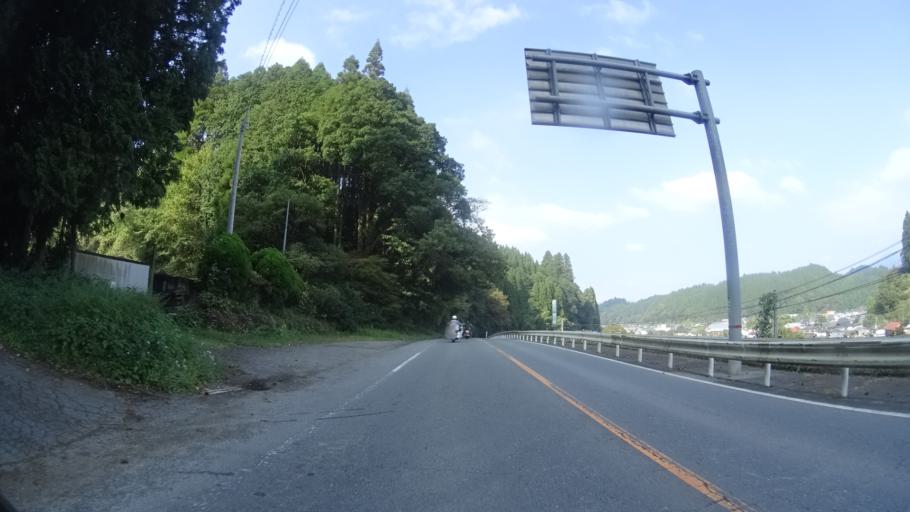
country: JP
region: Kumamoto
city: Aso
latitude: 33.0937
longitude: 131.0662
